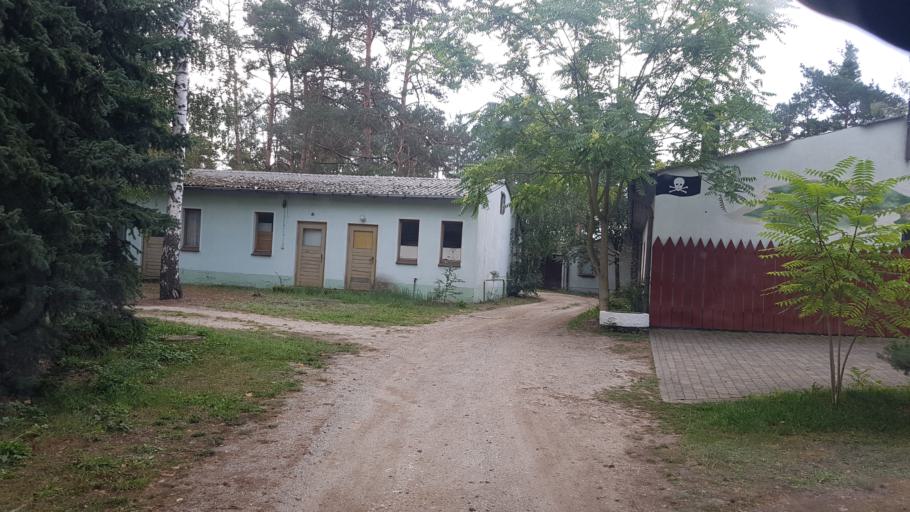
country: DE
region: Brandenburg
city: Ruckersdorf
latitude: 51.5744
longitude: 13.5794
